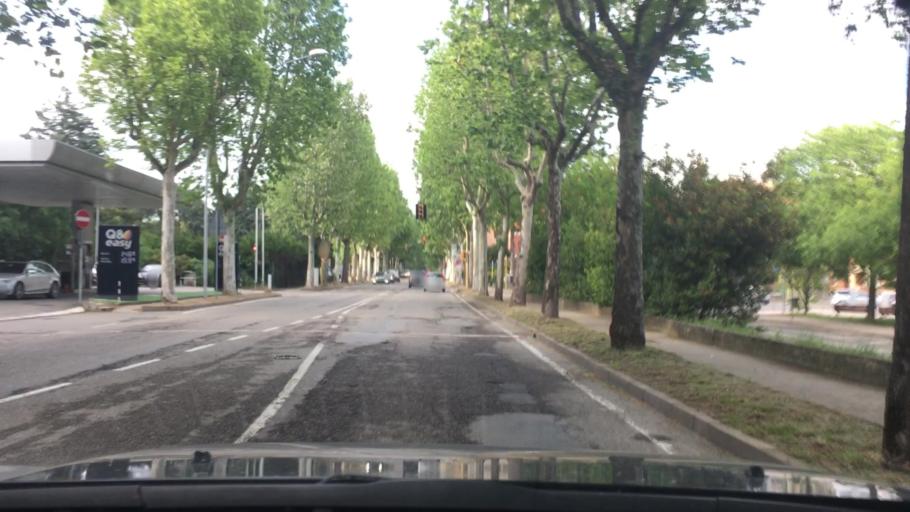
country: IT
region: Emilia-Romagna
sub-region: Provincia di Bologna
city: Sasso Marconi
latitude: 44.3923
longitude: 11.2463
